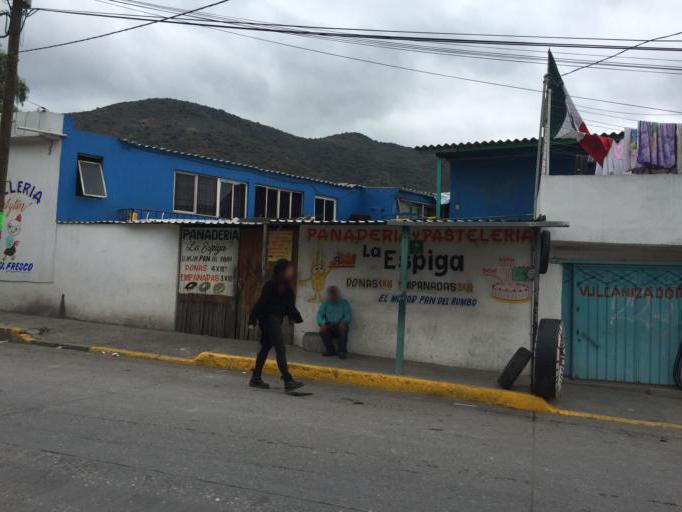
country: MX
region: Mexico
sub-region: Tlalnepantla de Baz
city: Puerto Escondido (Tepeolulco Puerto Escondido)
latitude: 19.5677
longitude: -99.0906
